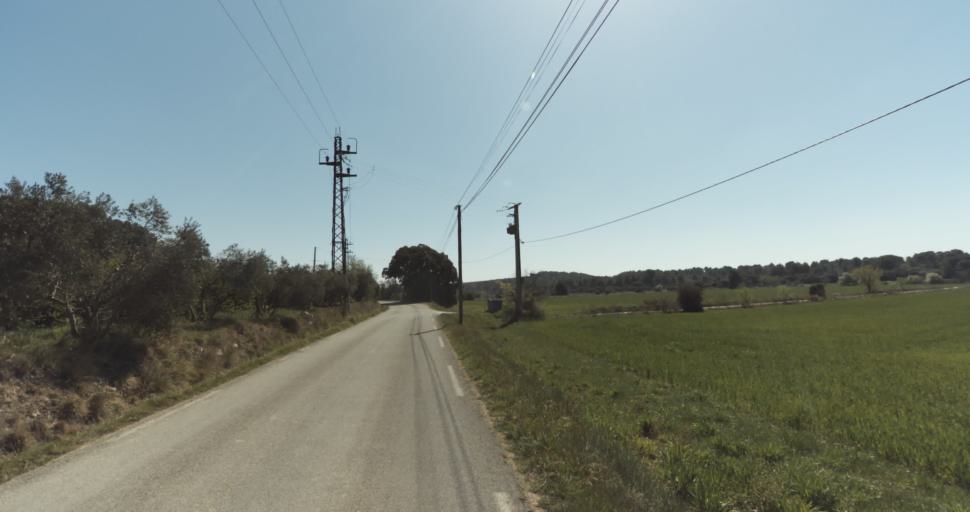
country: FR
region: Provence-Alpes-Cote d'Azur
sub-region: Departement des Bouches-du-Rhone
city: Pelissanne
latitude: 43.6118
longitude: 5.1748
